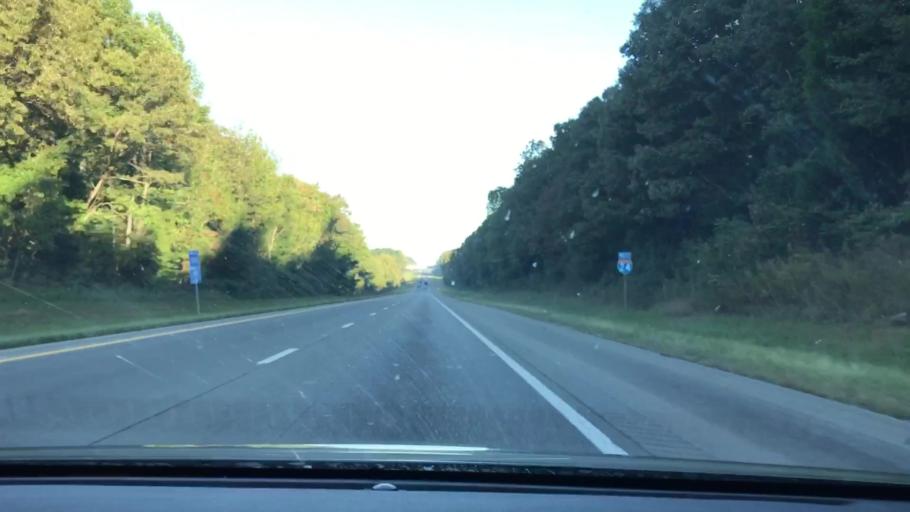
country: US
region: Tennessee
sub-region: Cheatham County
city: Pleasant View
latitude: 36.4563
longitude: -87.1081
